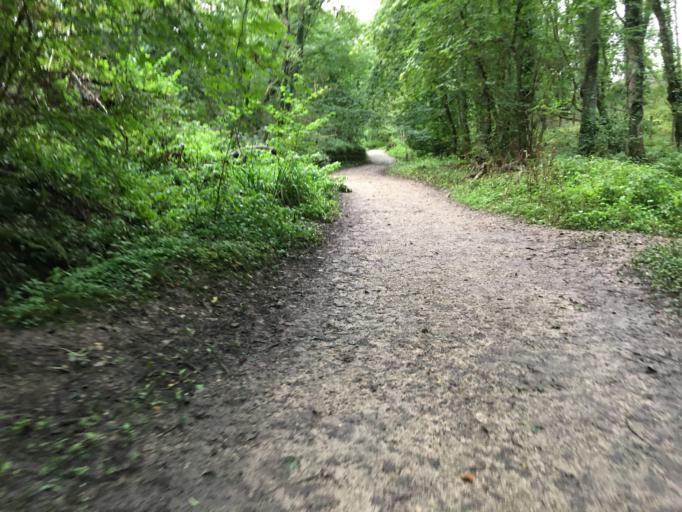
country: GB
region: England
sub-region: North Yorkshire
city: Sleights
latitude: 54.4051
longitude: -0.7283
